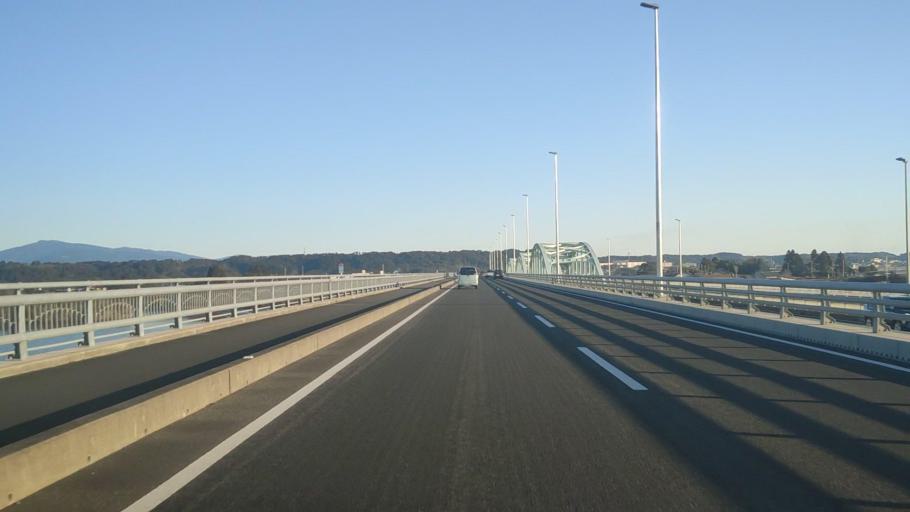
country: JP
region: Miyazaki
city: Tsuma
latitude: 32.0487
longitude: 131.4717
